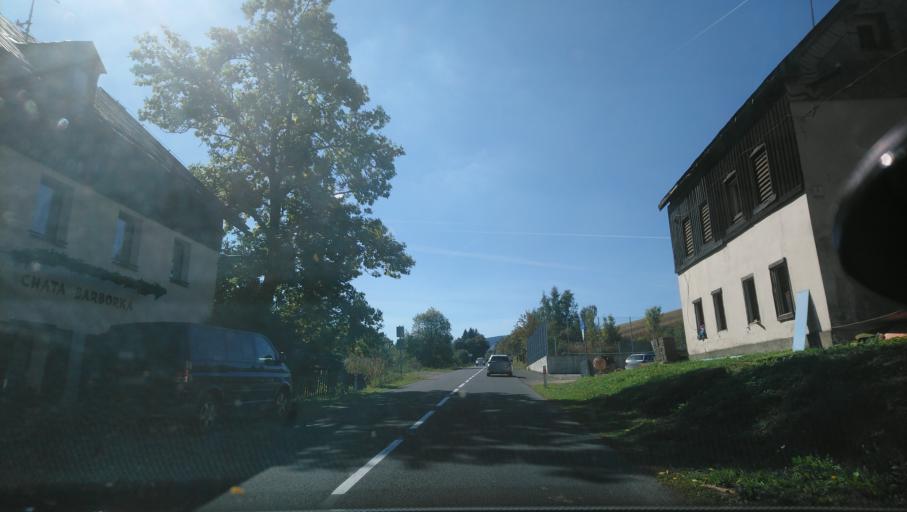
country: DE
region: Saxony
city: Kurort Oberwiesenthal
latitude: 50.4271
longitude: 13.0017
